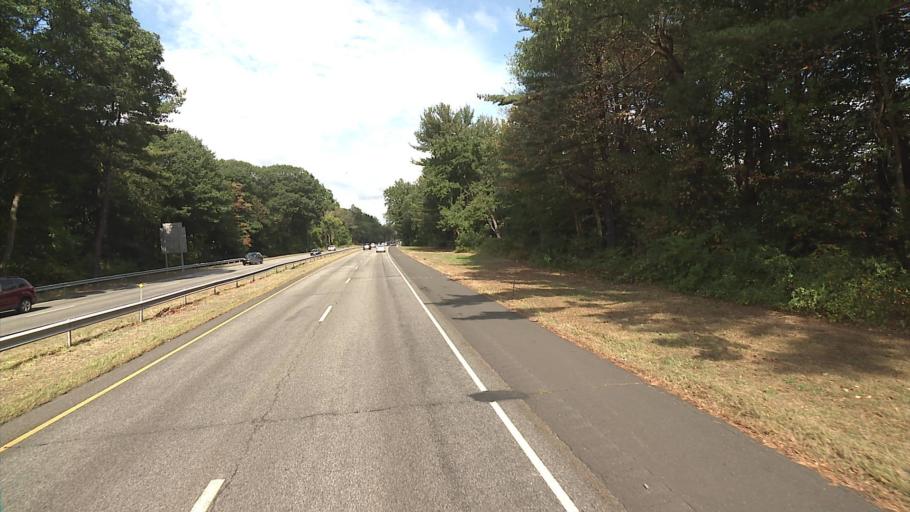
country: US
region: Connecticut
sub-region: New Haven County
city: Wallingford
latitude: 41.4811
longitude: -72.8215
